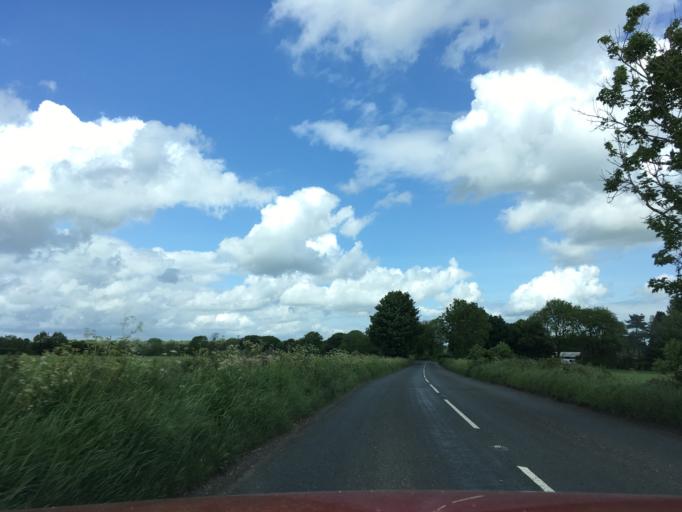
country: GB
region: England
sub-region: Gloucestershire
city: Shurdington
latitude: 51.7977
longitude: -2.1263
